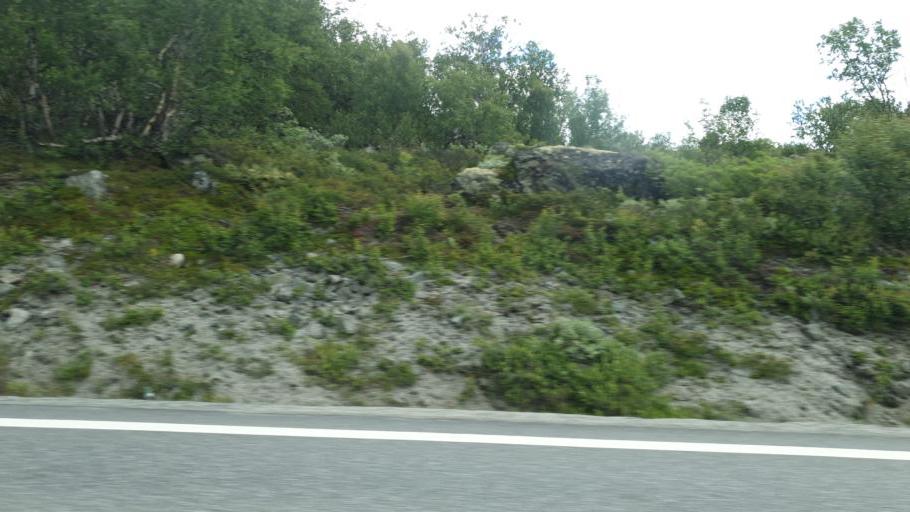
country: NO
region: Sor-Trondelag
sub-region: Oppdal
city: Oppdal
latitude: 62.2704
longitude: 9.5834
